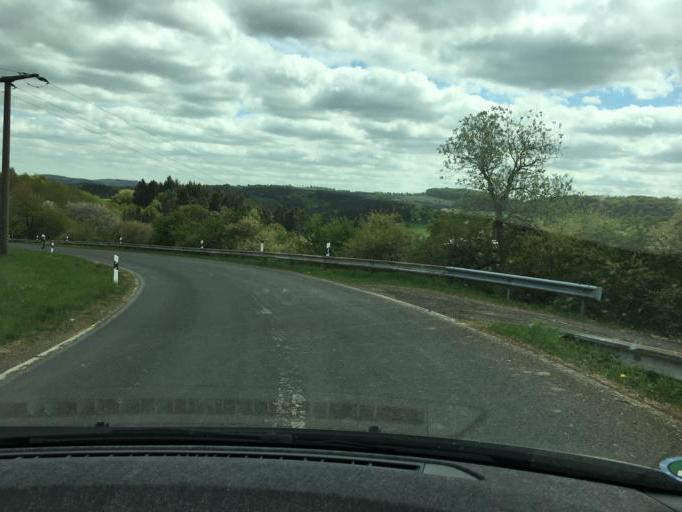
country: DE
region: Rheinland-Pfalz
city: Kirchsahr
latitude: 50.5021
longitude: 6.9029
